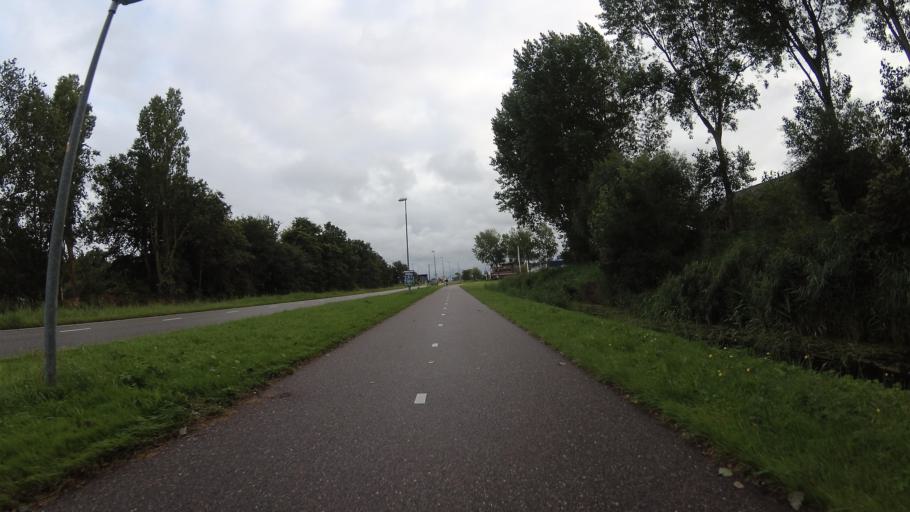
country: NL
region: North Holland
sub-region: Gemeente Den Helder
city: Den Helder
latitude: 52.9376
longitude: 4.7568
